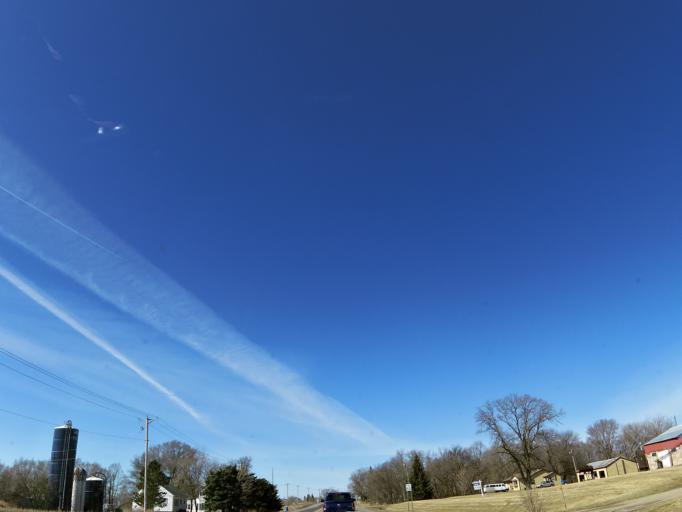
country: US
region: Minnesota
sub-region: Hennepin County
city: Maple Plain
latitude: 45.0655
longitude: -93.6405
